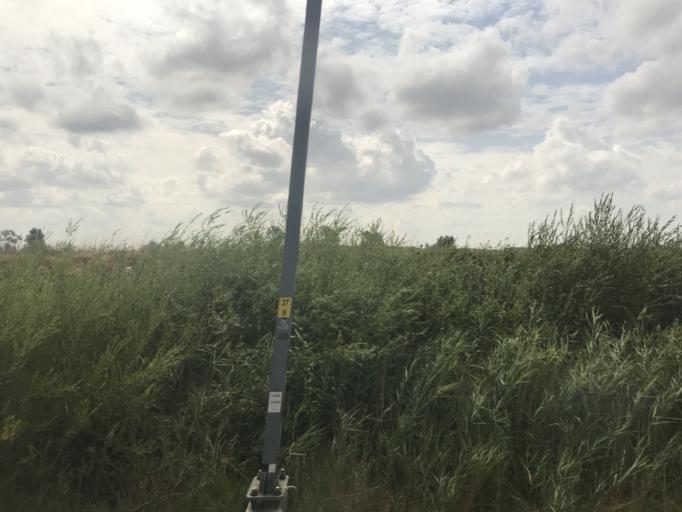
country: PL
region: Greater Poland Voivodeship
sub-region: Powiat gnieznienski
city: Lubowo
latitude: 52.5080
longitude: 17.5001
